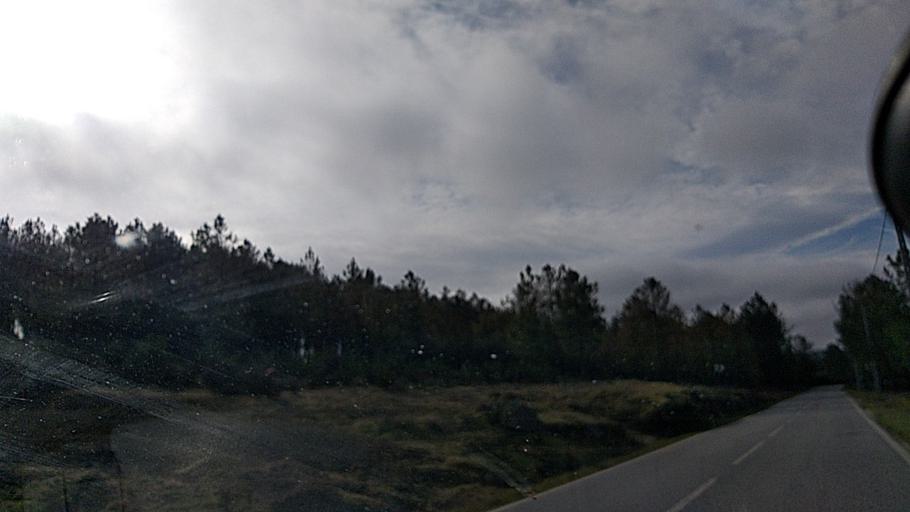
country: PT
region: Guarda
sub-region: Aguiar da Beira
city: Aguiar da Beira
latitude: 40.7778
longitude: -7.5182
